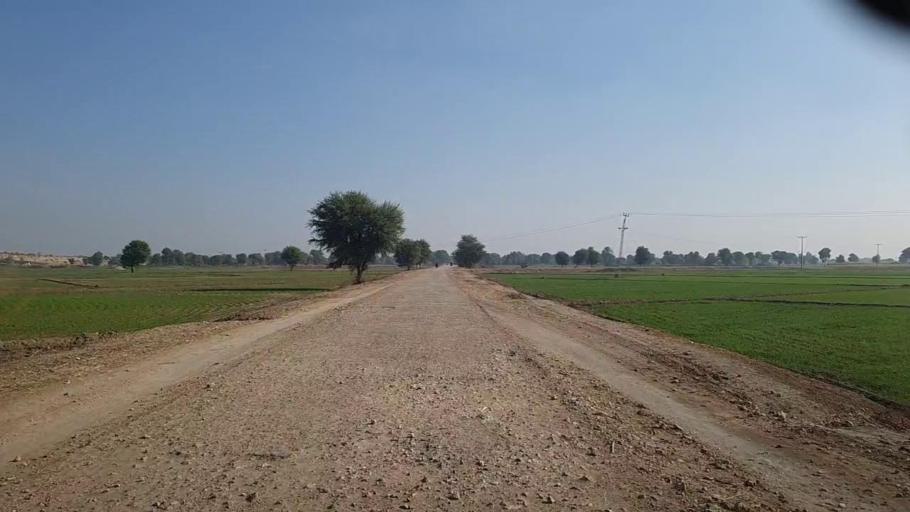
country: PK
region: Sindh
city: Darya Khan Marri
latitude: 26.6669
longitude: 68.3350
